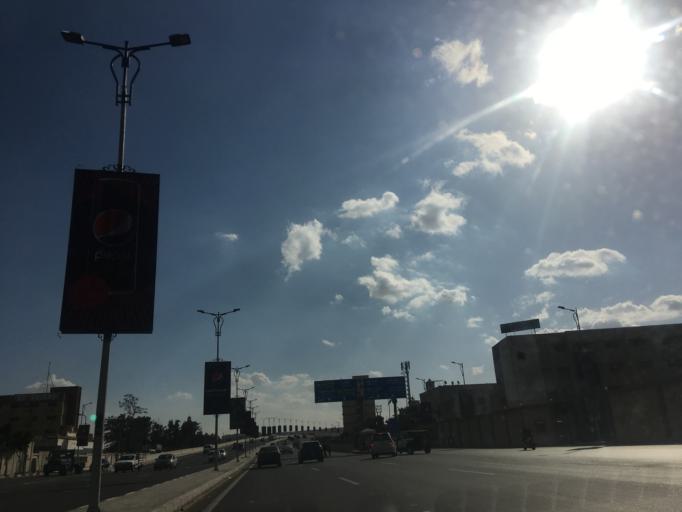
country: EG
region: Muhafazat al Qahirah
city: Cairo
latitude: 30.0471
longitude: 31.3075
